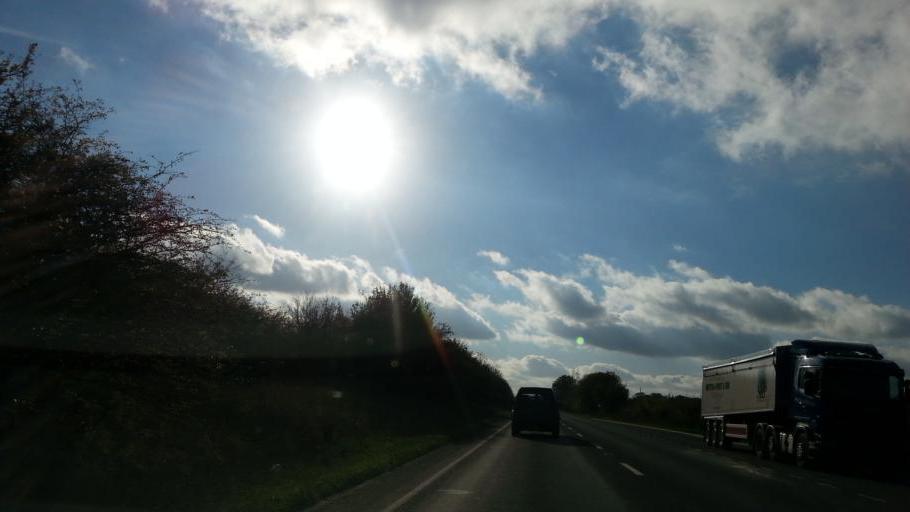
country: GB
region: England
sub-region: Norfolk
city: Harleston
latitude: 52.3826
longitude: 1.2599
